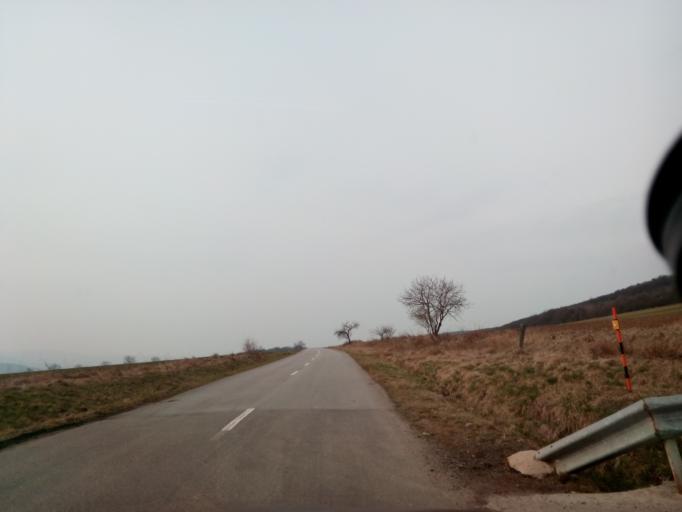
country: HU
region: Borsod-Abauj-Zemplen
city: Satoraljaujhely
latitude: 48.4709
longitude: 21.6761
